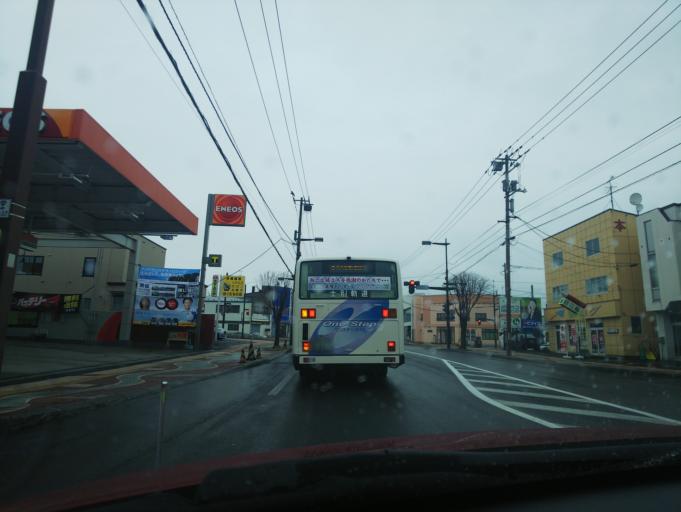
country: JP
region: Hokkaido
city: Nayoro
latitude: 44.1725
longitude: 142.3933
